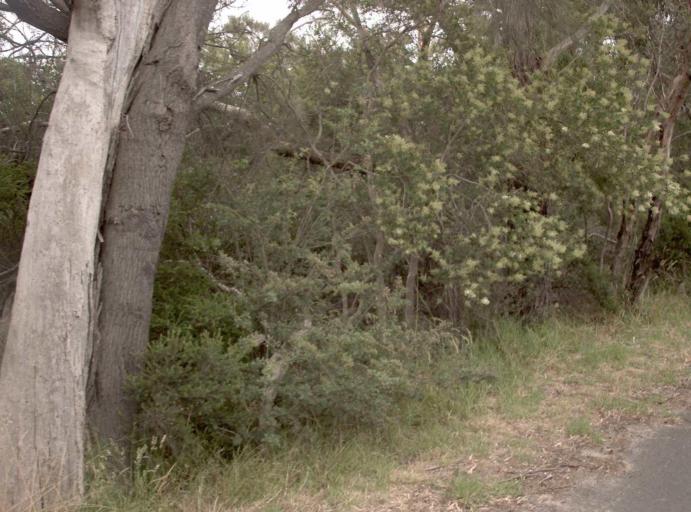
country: AU
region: Victoria
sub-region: Mornington Peninsula
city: Mount Martha
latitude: -38.2661
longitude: 145.0370
